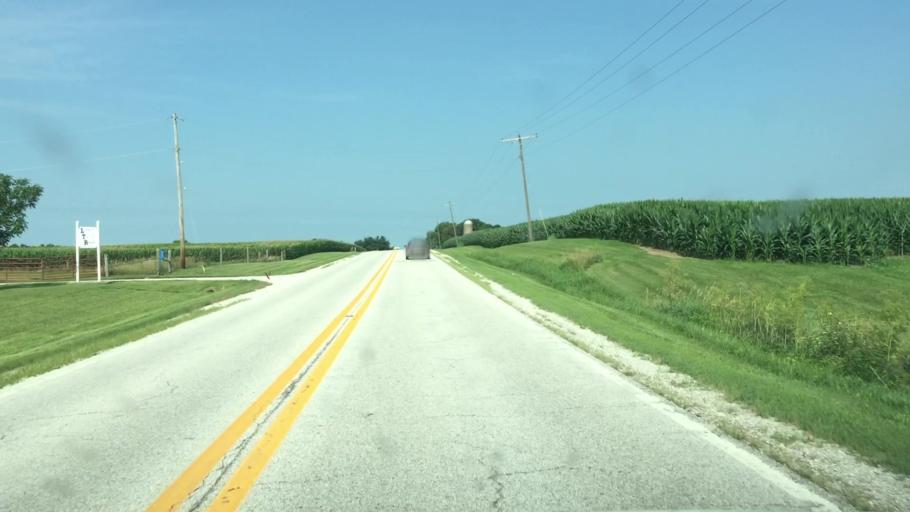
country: US
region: Illinois
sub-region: Hancock County
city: Nauvoo
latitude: 40.5518
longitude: -91.3328
